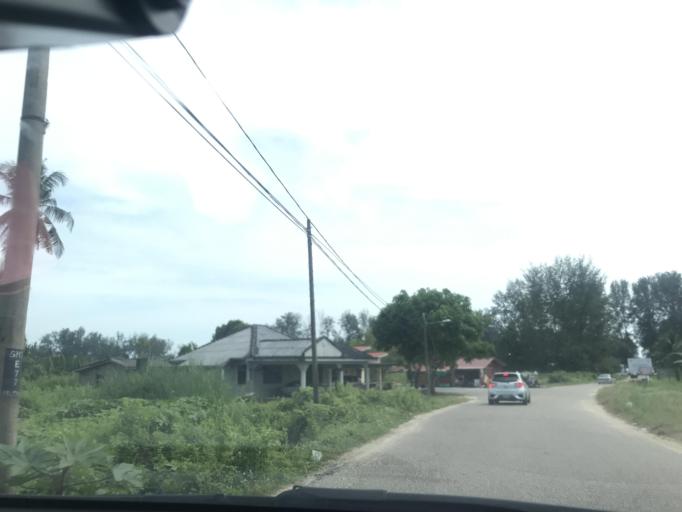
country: MY
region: Kelantan
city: Tumpat
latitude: 6.2203
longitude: 102.1190
